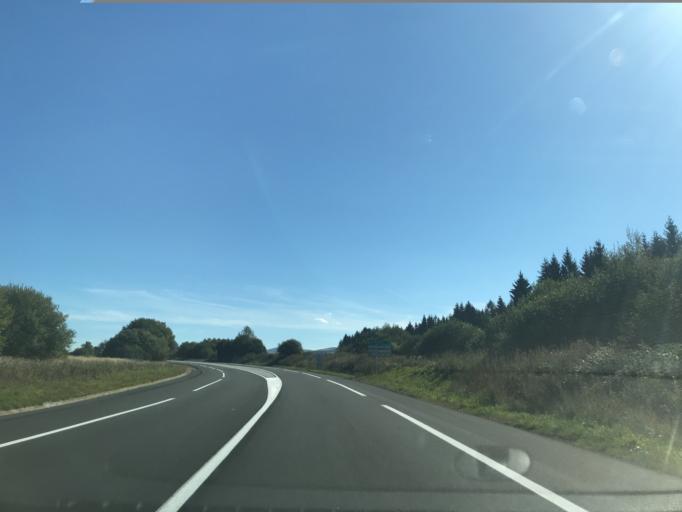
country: FR
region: Auvergne
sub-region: Departement du Puy-de-Dome
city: Saint-Sauves-d'Auvergne
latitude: 45.6548
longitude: 2.6936
